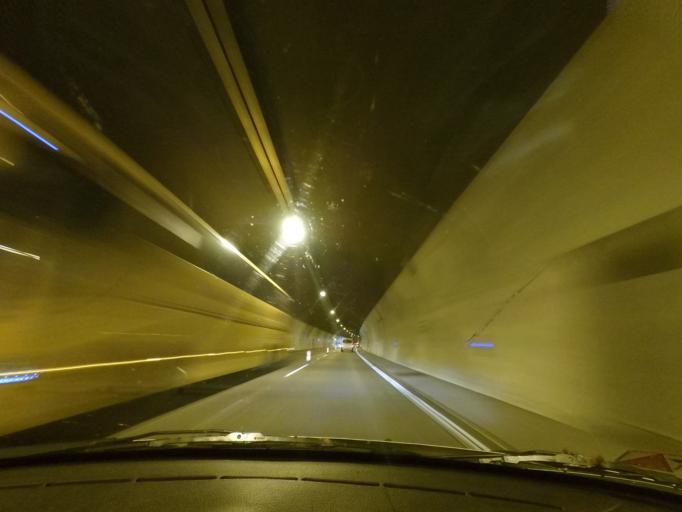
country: CZ
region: Ustecky
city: Libouchec
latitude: 50.7557
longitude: 13.9850
